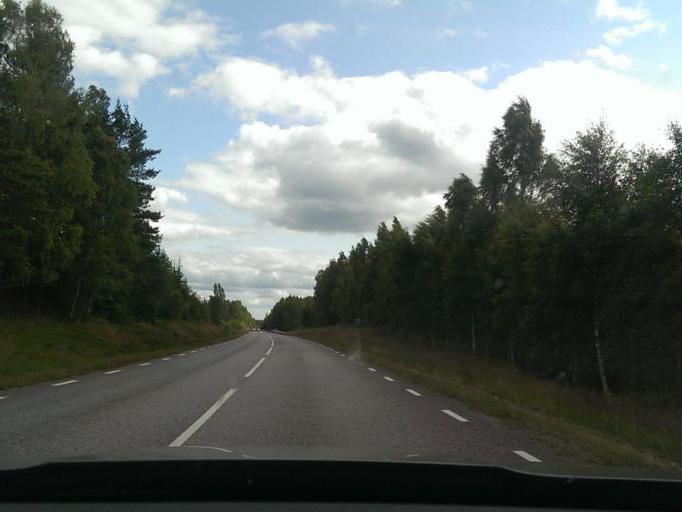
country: SE
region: Kronoberg
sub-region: Ljungby Kommun
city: Lagan
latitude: 56.9316
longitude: 13.9801
